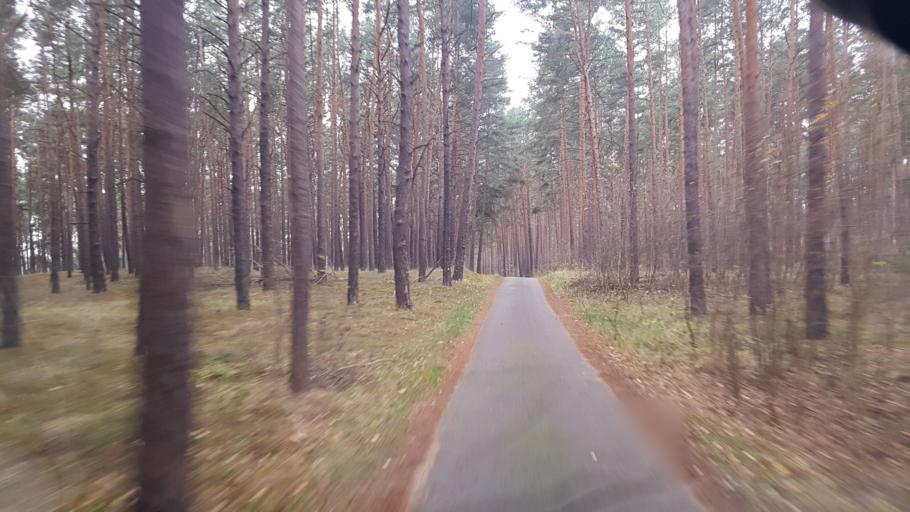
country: DE
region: Brandenburg
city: Schenkendobern
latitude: 51.9770
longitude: 14.6556
